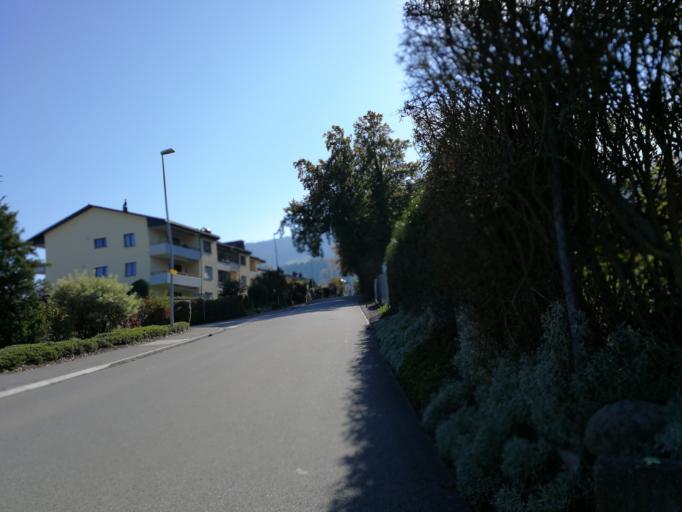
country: CH
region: Schwyz
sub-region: Bezirk March
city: Altendorf
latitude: 47.1893
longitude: 8.8262
